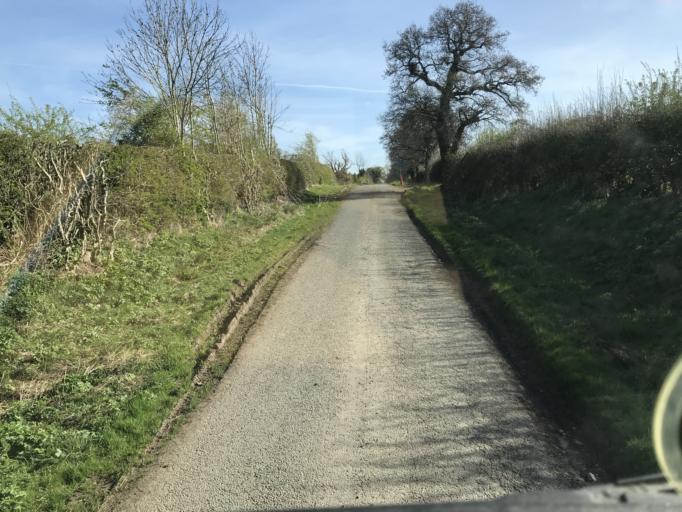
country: GB
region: England
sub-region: Cheshire East
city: Middlewich
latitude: 53.2296
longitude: -2.4694
